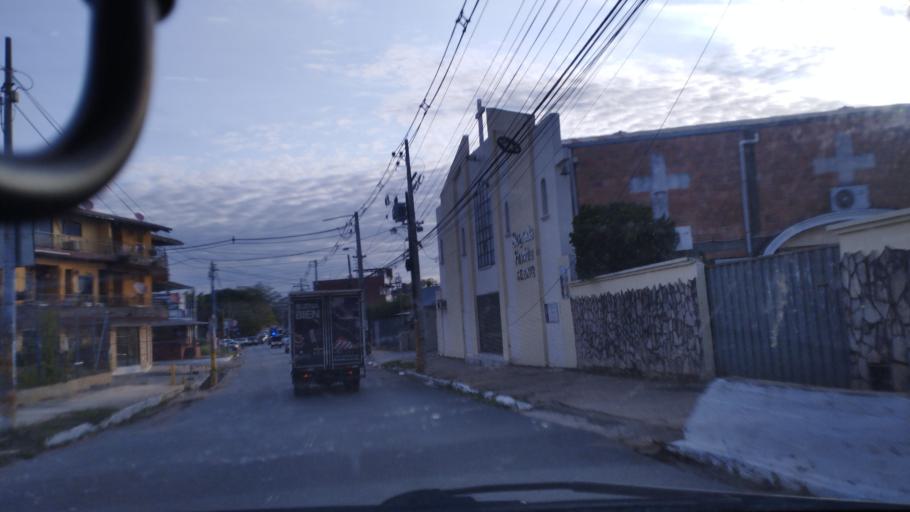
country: PY
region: Central
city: Fernando de la Mora
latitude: -25.3179
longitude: -57.5499
